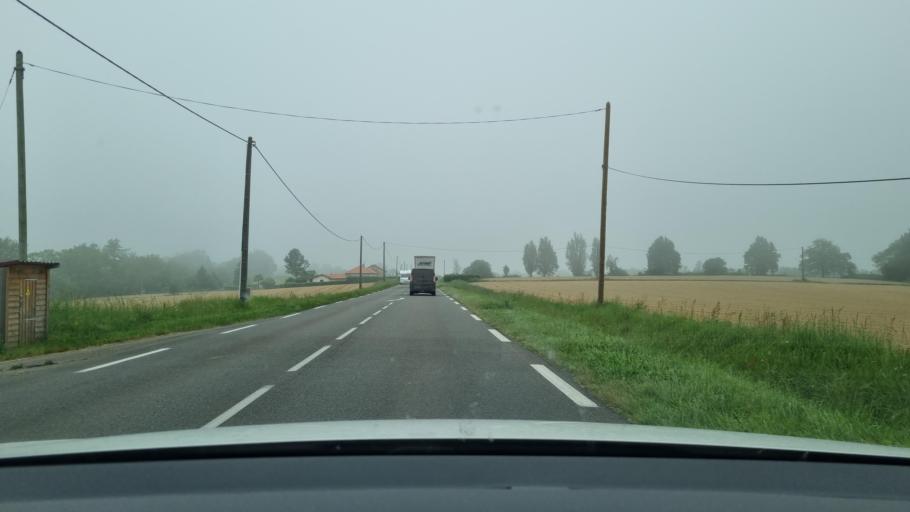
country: FR
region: Aquitaine
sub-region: Departement des Landes
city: Hagetmau
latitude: 43.6712
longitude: -0.5871
